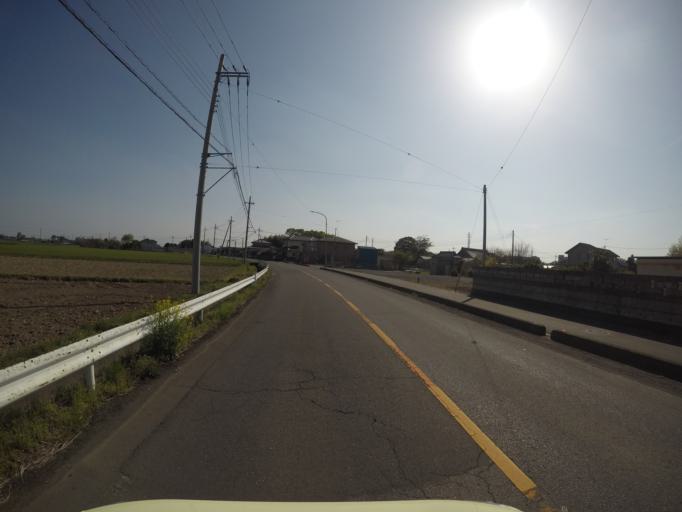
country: JP
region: Ibaraki
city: Yuki
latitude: 36.3329
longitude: 139.8884
